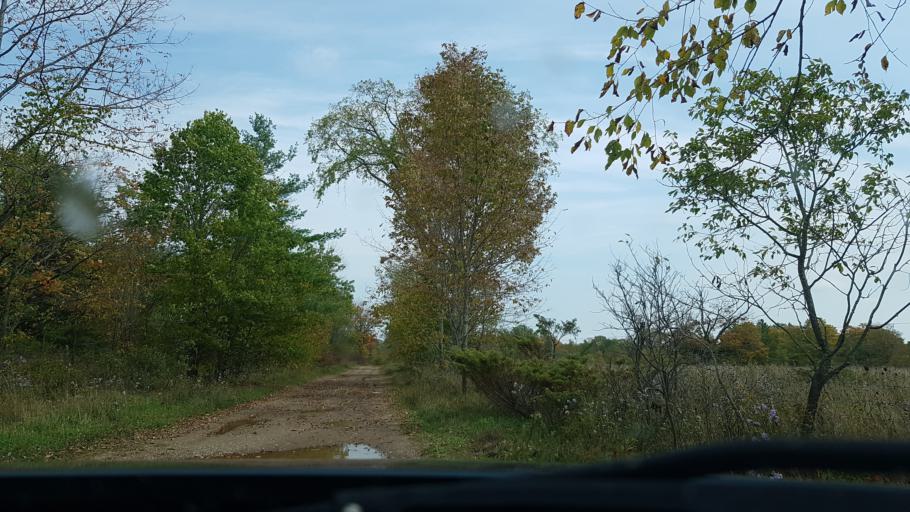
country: CA
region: Ontario
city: Orillia
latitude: 44.6902
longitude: -79.0298
